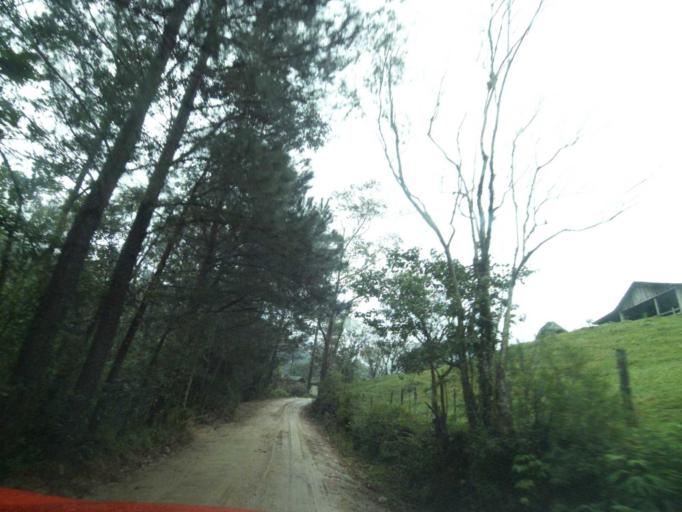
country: BR
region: Santa Catarina
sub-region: Anitapolis
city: Anitapolis
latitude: -27.9059
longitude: -49.1953
